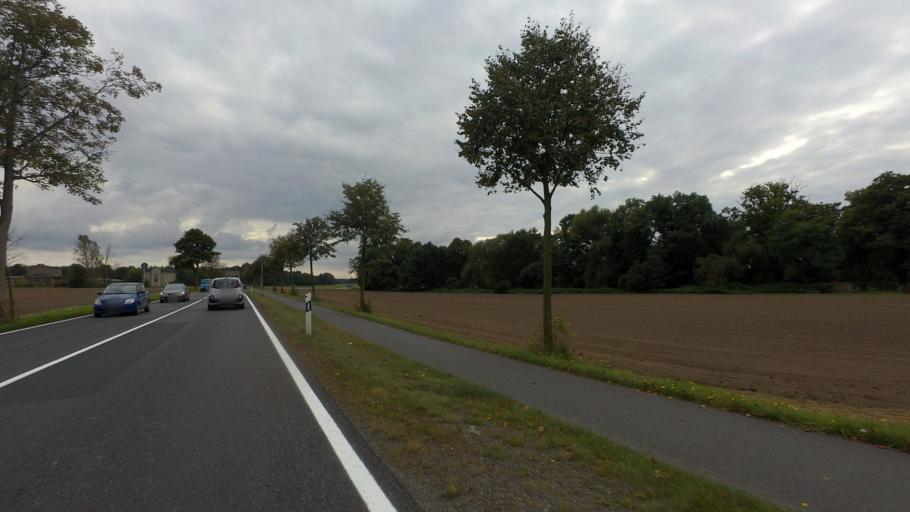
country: DE
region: Saxony
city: Konigswartha
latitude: 51.3038
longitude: 14.3271
